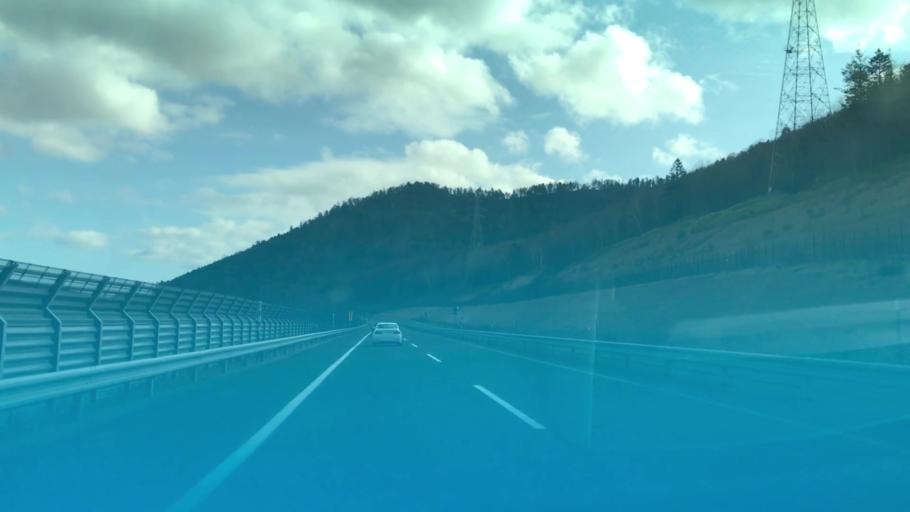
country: JP
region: Hokkaido
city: Shimo-furano
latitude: 43.0533
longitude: 142.5807
